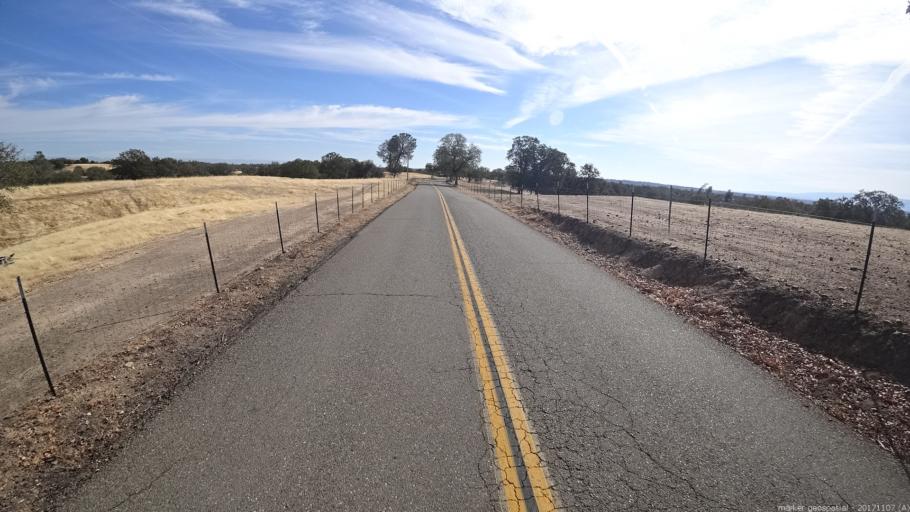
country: US
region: California
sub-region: Shasta County
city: Shasta
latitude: 40.4334
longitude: -122.5227
